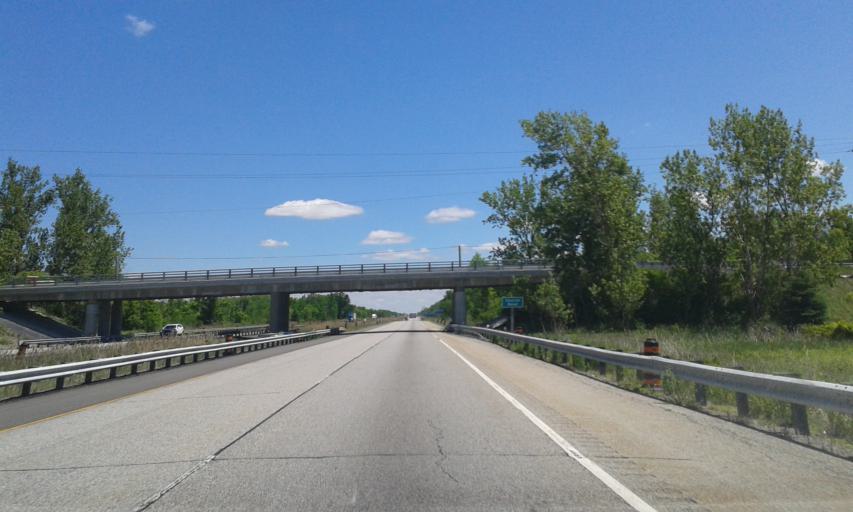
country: US
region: New York
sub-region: St. Lawrence County
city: Norfolk
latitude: 44.9377
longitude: -75.1487
